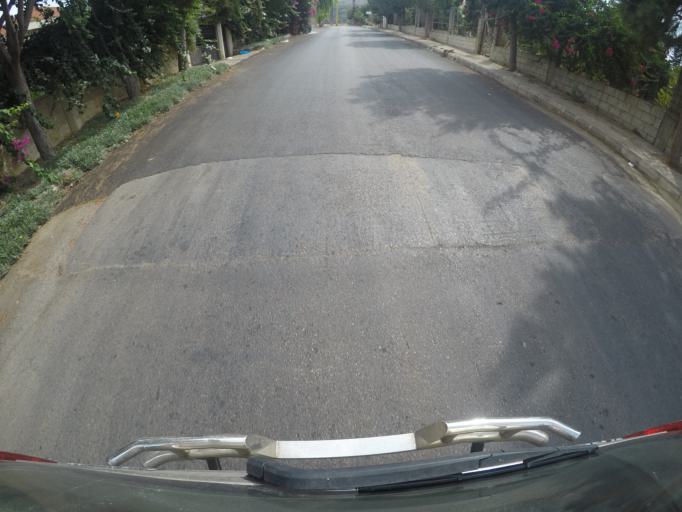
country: LB
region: Mont-Liban
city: Beit ed Dine
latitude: 33.7331
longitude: 35.4595
